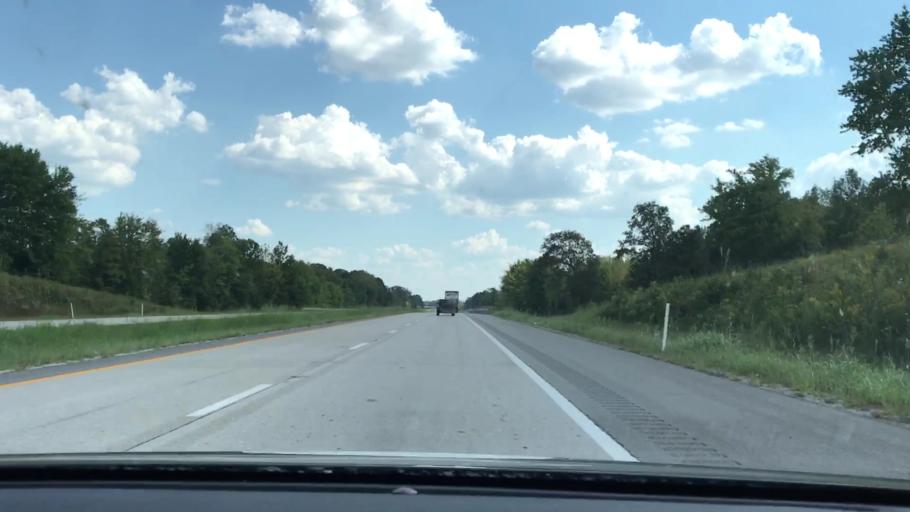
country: US
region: Kentucky
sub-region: Ohio County
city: Oak Grove
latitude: 37.3653
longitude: -86.7972
